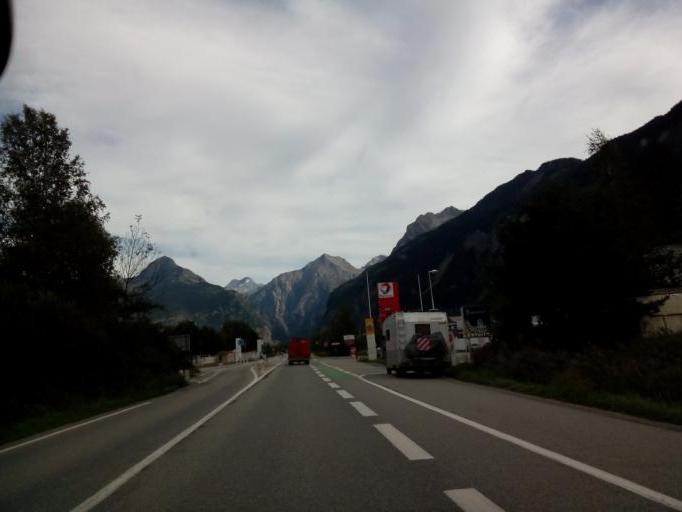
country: FR
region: Rhone-Alpes
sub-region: Departement de l'Isere
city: Huez
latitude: 45.0676
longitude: 6.0213
